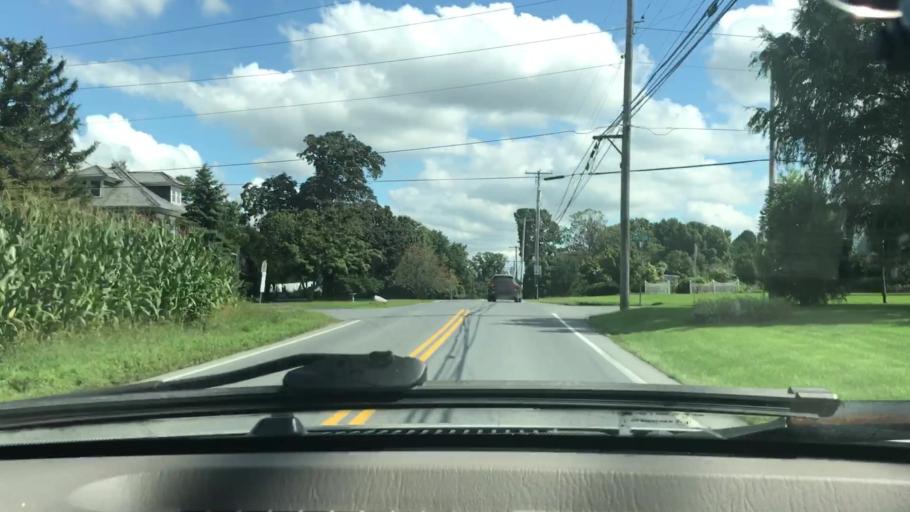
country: US
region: Pennsylvania
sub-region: Lancaster County
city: Landisville
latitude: 40.1139
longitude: -76.3867
